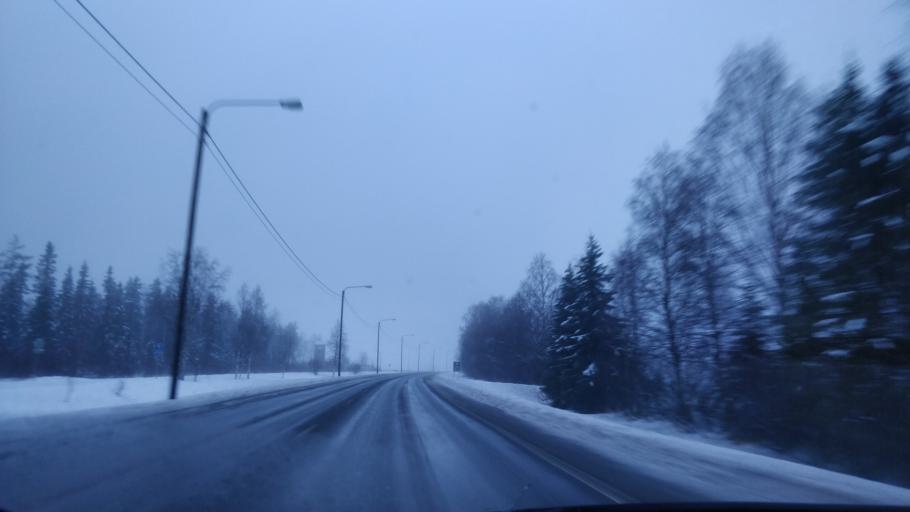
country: FI
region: Lapland
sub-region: Kemi-Tornio
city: Tervola
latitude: 66.1498
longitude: 24.9770
